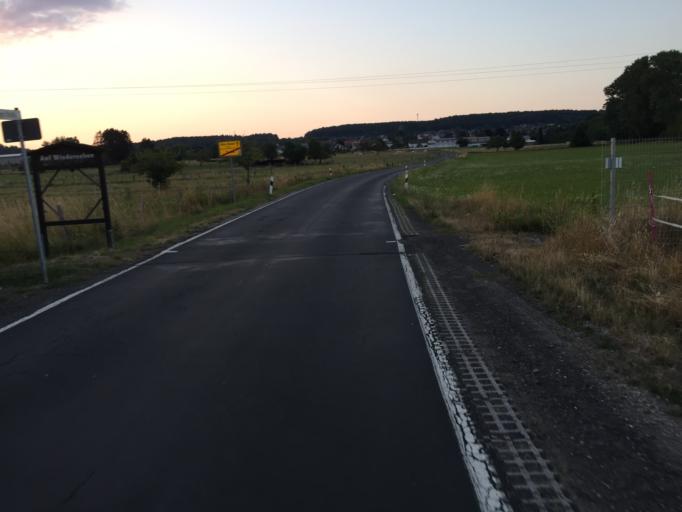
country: DE
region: Hesse
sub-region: Regierungsbezirk Giessen
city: Alten Buseck
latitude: 50.6119
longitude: 8.7520
